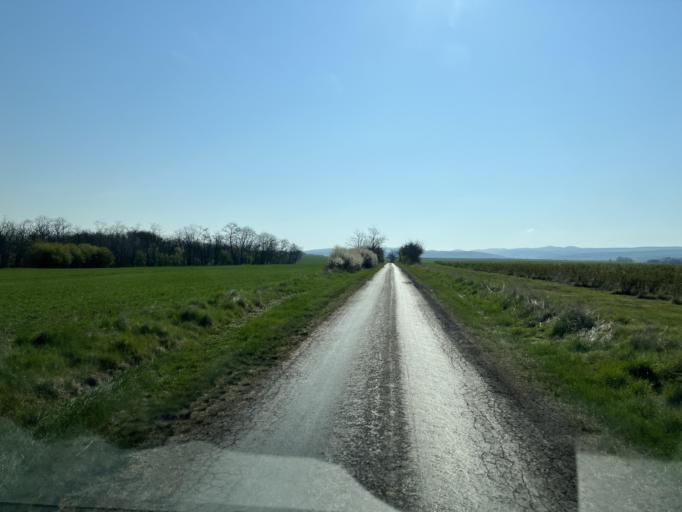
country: SK
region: Nitriansky
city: Sahy
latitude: 48.0497
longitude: 18.8617
